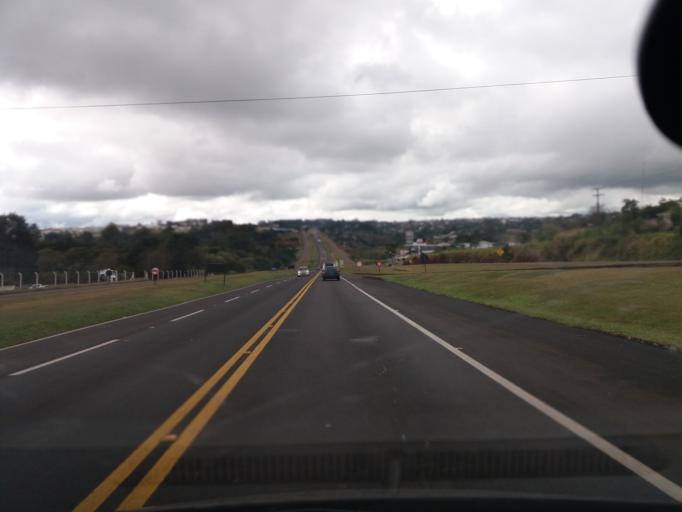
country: BR
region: Parana
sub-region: Cascavel
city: Cascavel
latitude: -24.9750
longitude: -53.4408
